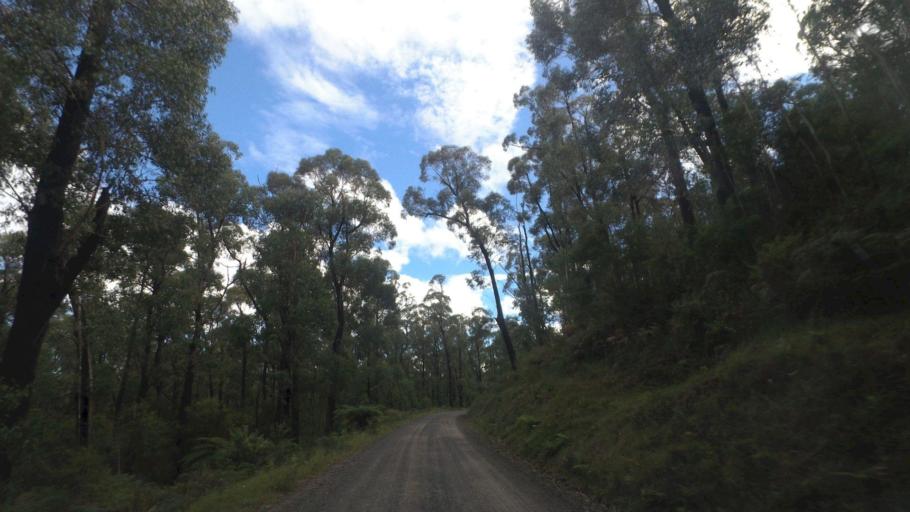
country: AU
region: Victoria
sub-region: Cardinia
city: Bunyip
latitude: -37.9957
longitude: 145.8149
